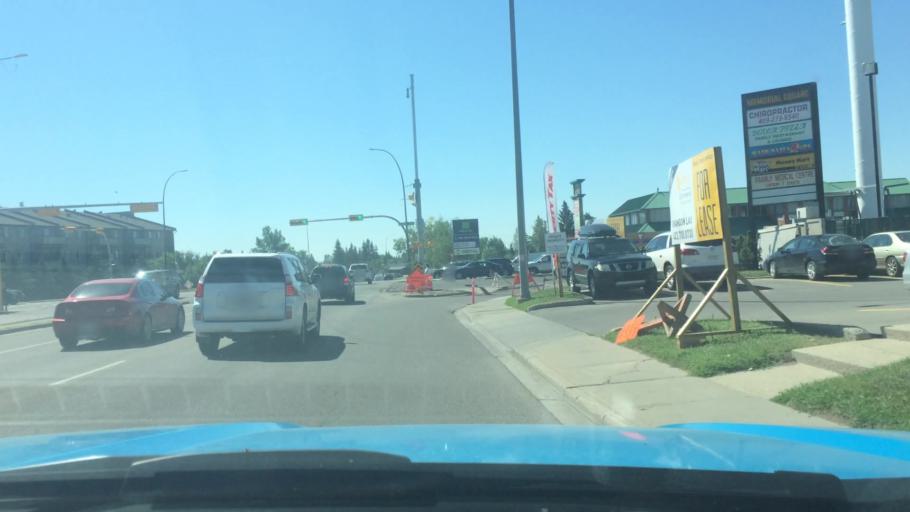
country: CA
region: Alberta
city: Calgary
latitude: 51.0539
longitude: -113.9562
